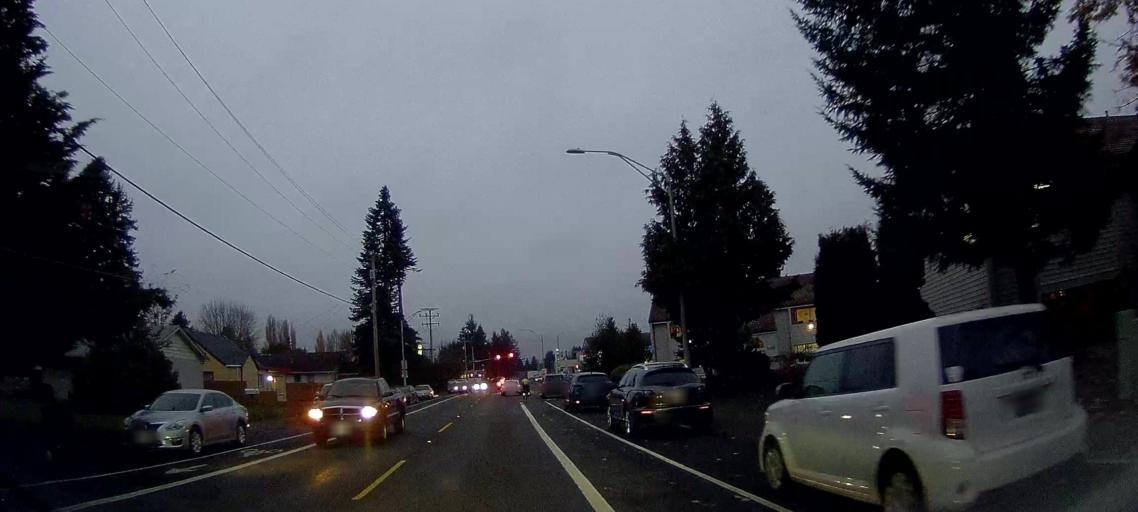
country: US
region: Washington
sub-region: Thurston County
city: Olympia
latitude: 47.0443
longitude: -122.8691
